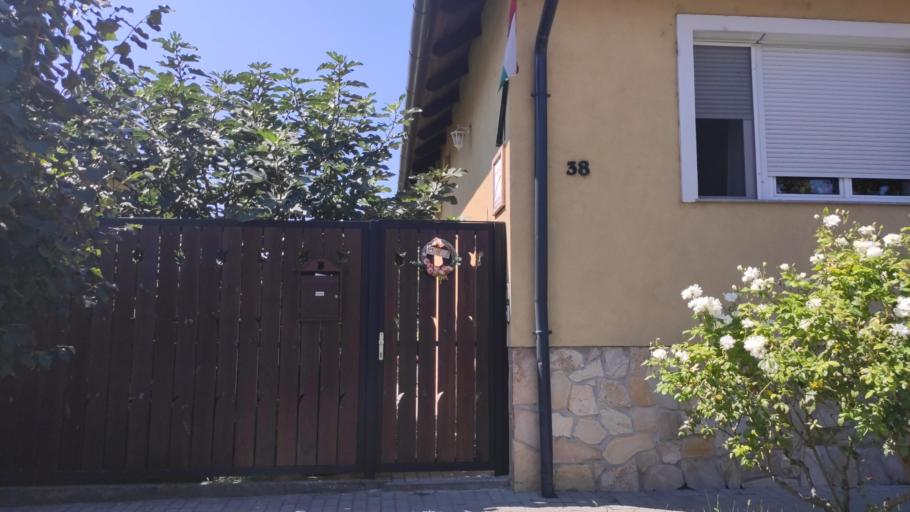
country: HU
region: Pest
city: Halasztelek
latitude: 47.3960
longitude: 18.9862
